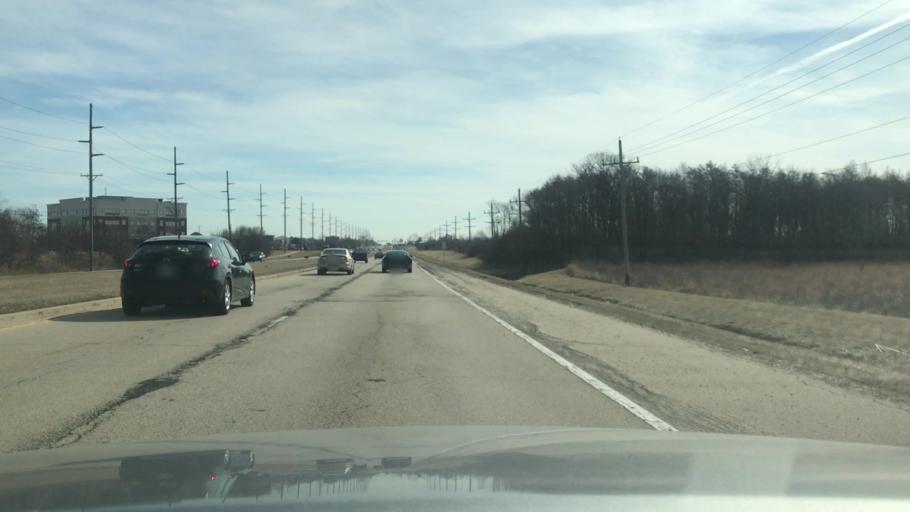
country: US
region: Illinois
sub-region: DuPage County
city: Naperville
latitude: 41.7474
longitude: -88.1796
